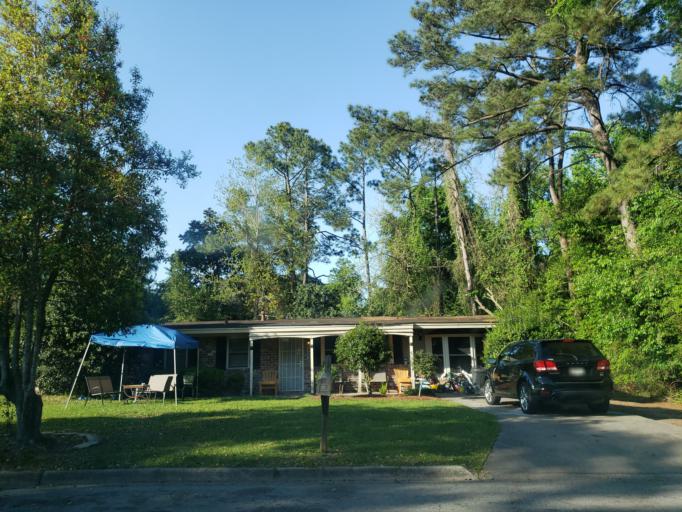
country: US
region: Georgia
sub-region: Chatham County
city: Thunderbolt
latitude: 32.0379
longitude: -81.0787
